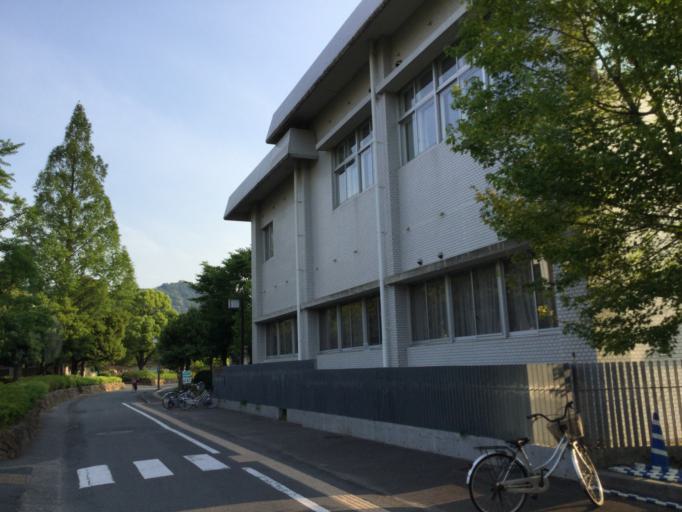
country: JP
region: Yamaguchi
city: Yamaguchi-shi
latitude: 34.1470
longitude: 131.4676
